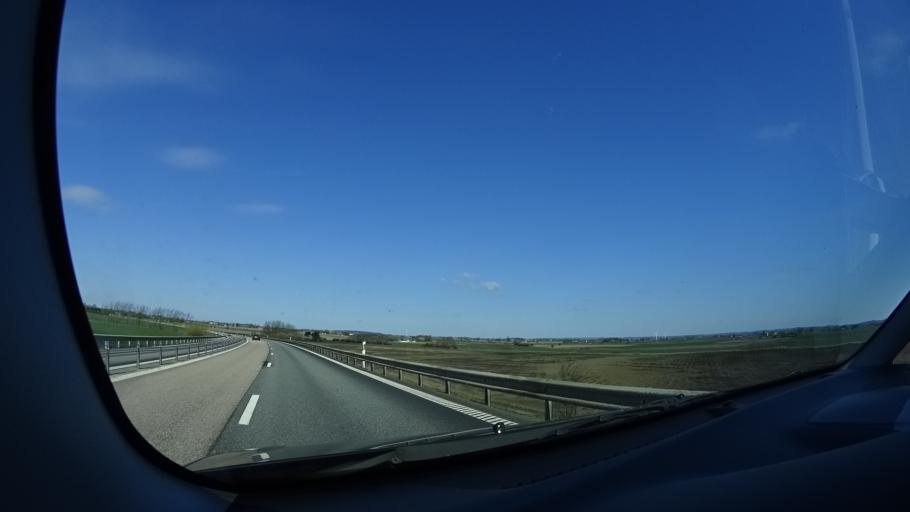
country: SE
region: Skane
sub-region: Astorps Kommun
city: Astorp
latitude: 56.1392
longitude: 12.9788
